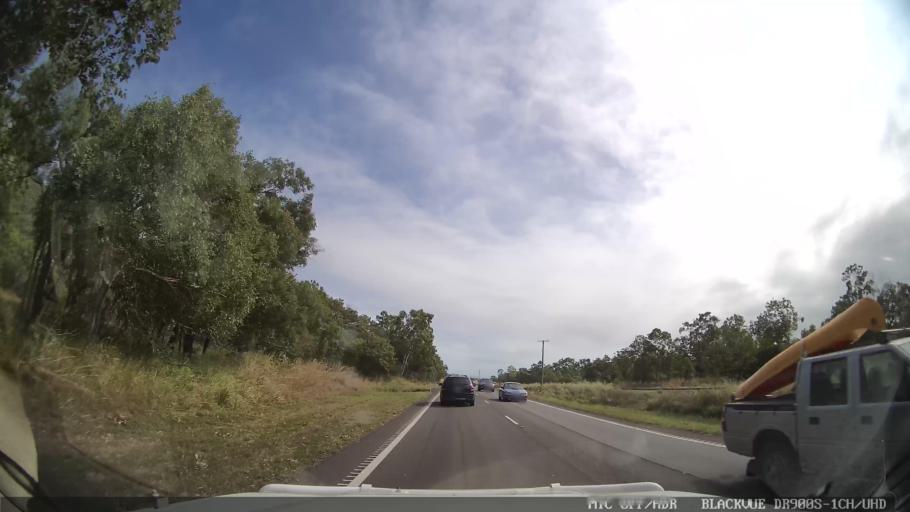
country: AU
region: Queensland
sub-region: Townsville
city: Townsville
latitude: -19.4029
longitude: 147.0265
